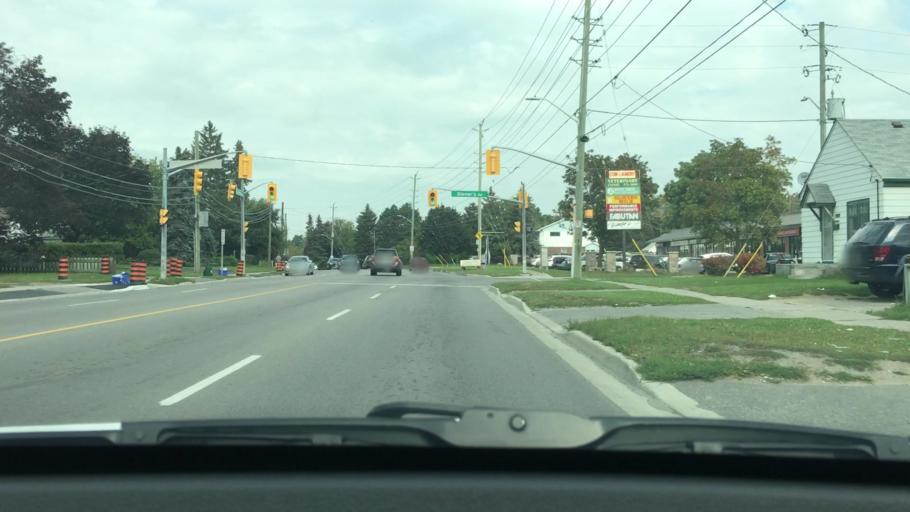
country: CA
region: Ontario
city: Oshawa
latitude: 43.9362
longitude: -78.8803
